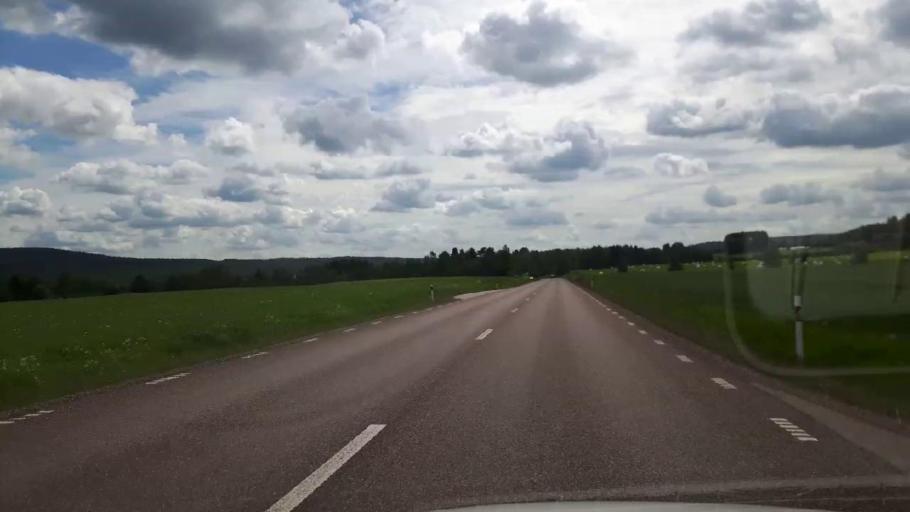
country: SE
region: Dalarna
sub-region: Hedemora Kommun
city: Langshyttan
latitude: 60.3873
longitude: 15.9040
